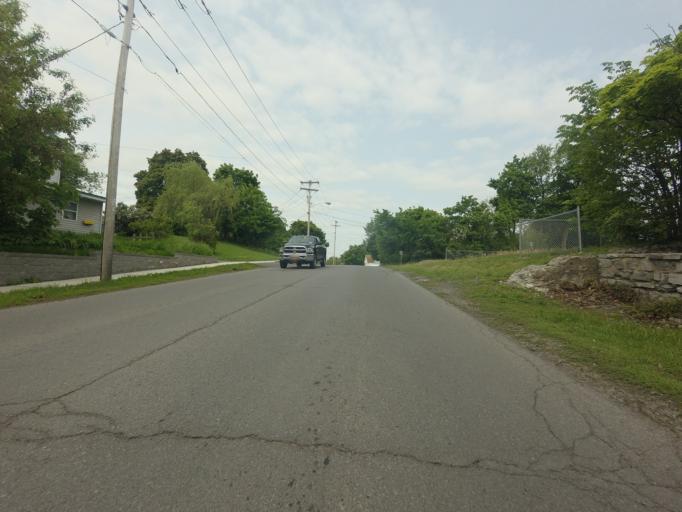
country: US
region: New York
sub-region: Jefferson County
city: Watertown
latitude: 43.9765
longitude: -75.8888
